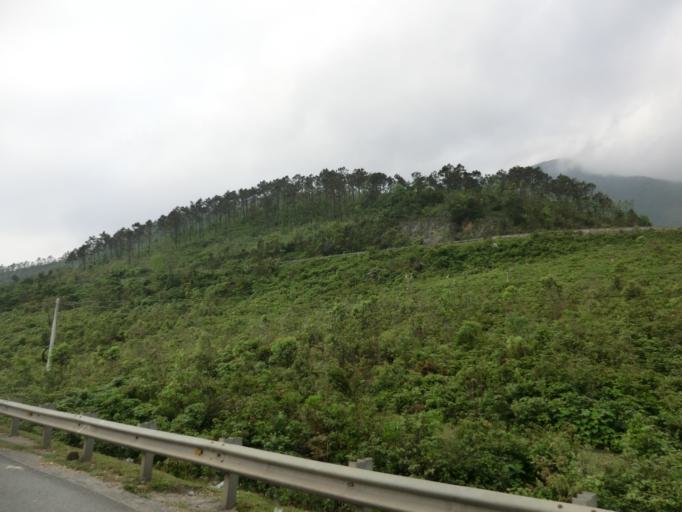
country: VN
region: Ha Tinh
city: Ky Anh
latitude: 17.9518
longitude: 106.4679
